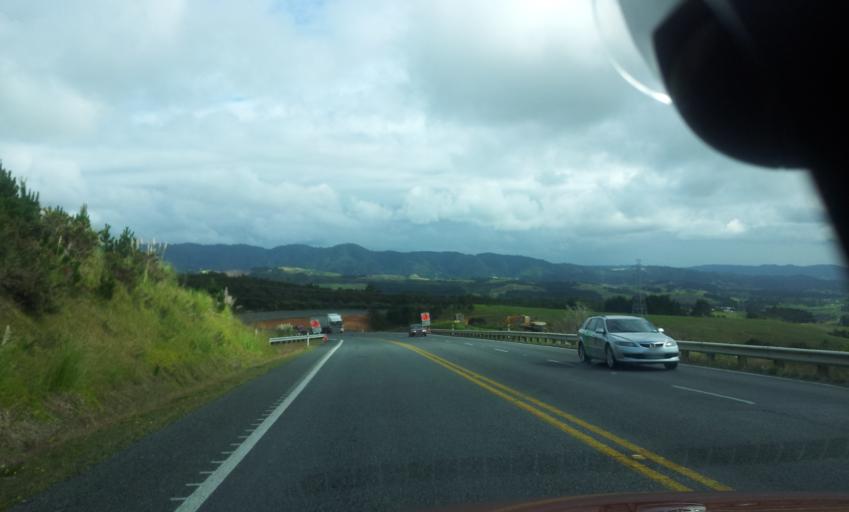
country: NZ
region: Northland
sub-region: Whangarei
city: Ruakaka
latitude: -36.0521
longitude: 174.4196
